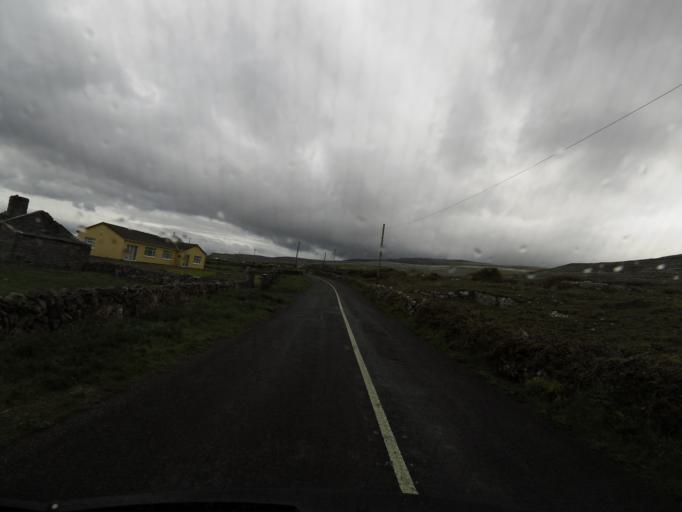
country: IE
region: Connaught
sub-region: County Galway
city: Bearna
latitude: 53.1216
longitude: -9.2789
